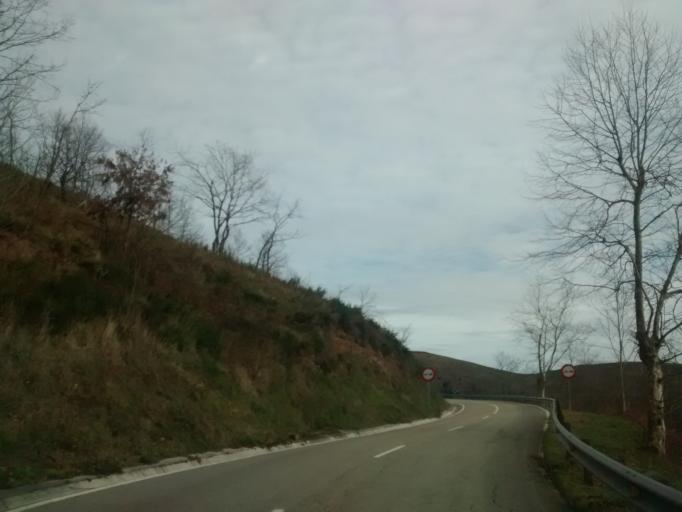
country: ES
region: Cantabria
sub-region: Provincia de Cantabria
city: Ruente
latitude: 43.2489
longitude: -4.3361
